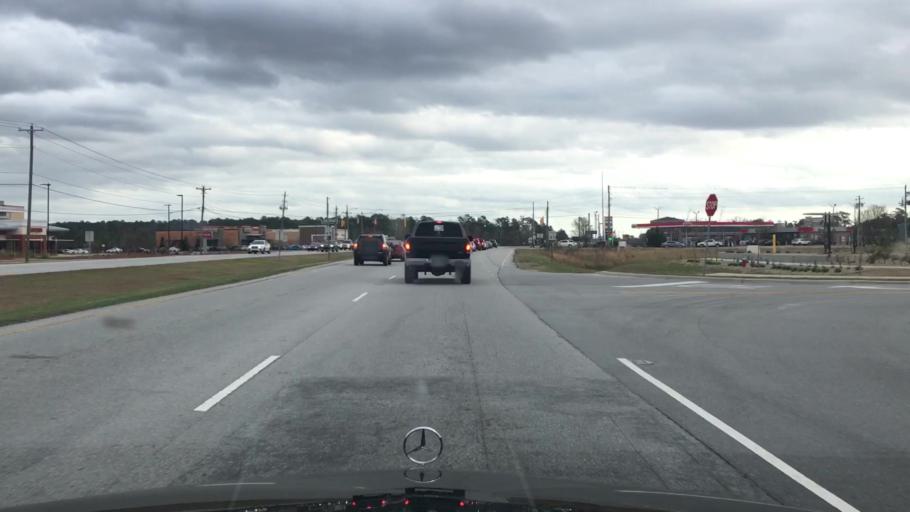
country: US
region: North Carolina
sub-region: Onslow County
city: Pumpkin Center
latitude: 34.7977
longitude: -77.4129
